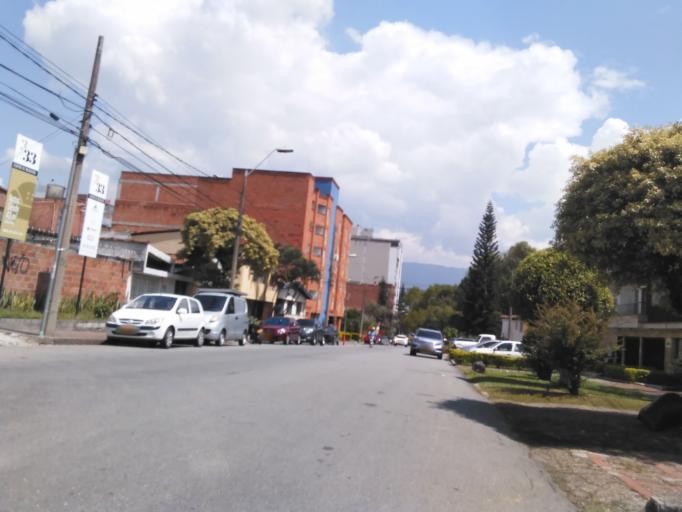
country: CO
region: Antioquia
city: Medellin
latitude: 6.2385
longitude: -75.5960
